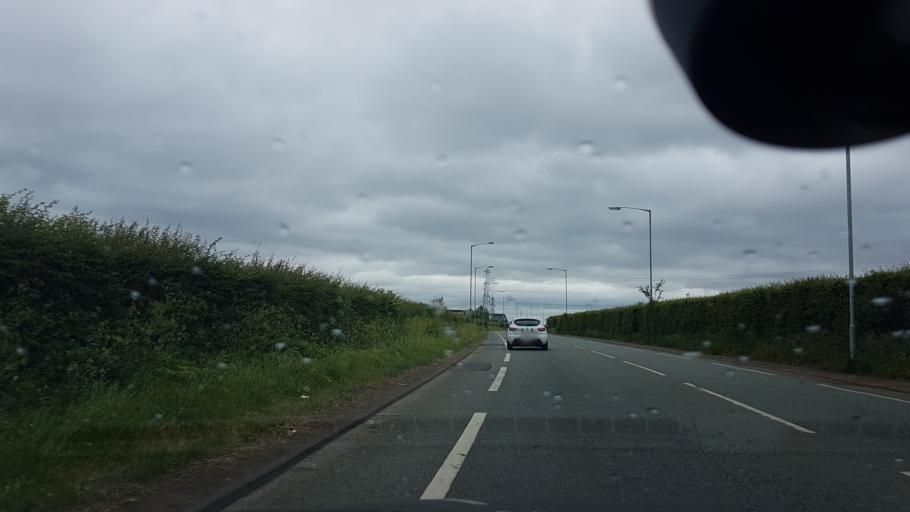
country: GB
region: England
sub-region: Borough of Bolton
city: Little Lever
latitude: 53.5796
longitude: -2.3532
